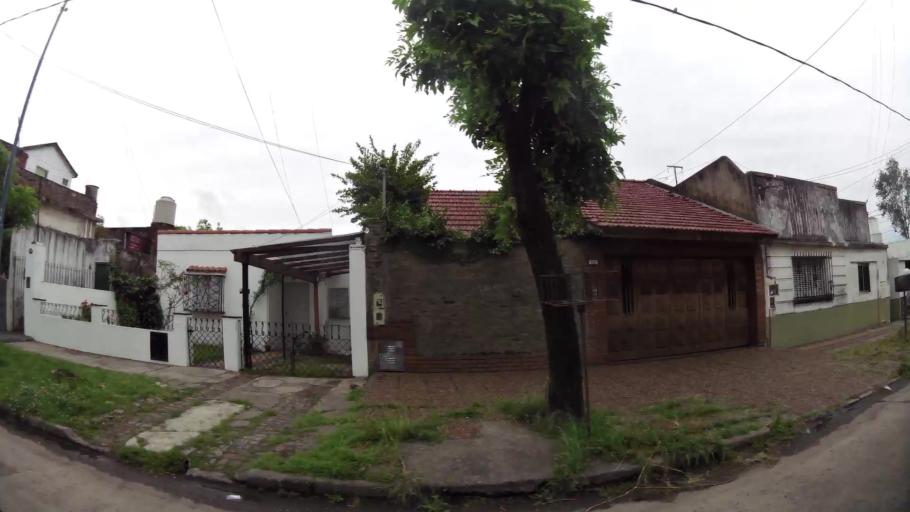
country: AR
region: Buenos Aires
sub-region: Partido de Lanus
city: Lanus
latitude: -34.7036
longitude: -58.3744
